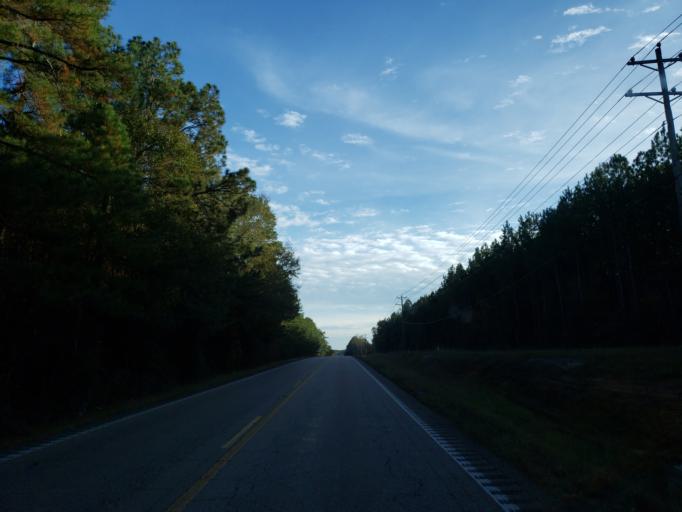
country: US
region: Mississippi
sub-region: Lamar County
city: West Hattiesburg
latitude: 31.3062
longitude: -89.4706
